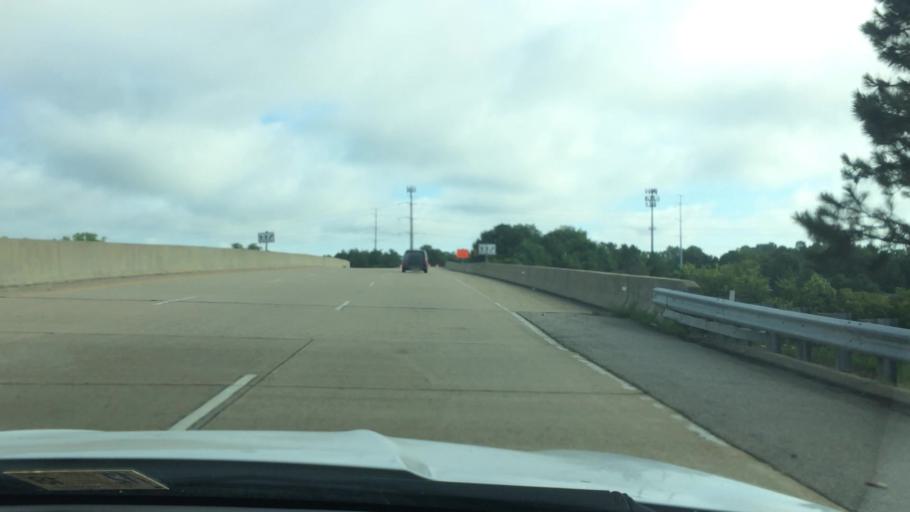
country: US
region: Virginia
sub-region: City of Williamsburg
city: Williamsburg
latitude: 37.2362
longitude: -76.6348
